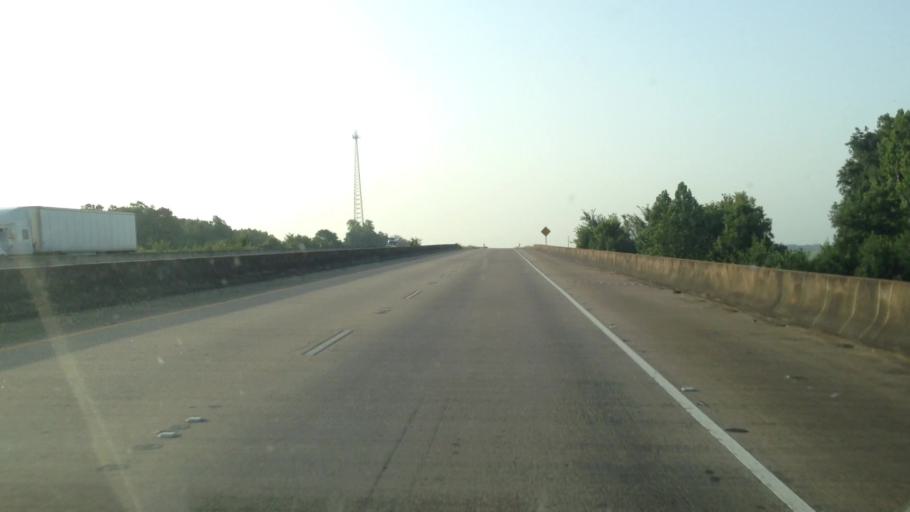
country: US
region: Louisiana
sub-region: Rapides Parish
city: Boyce
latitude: 31.3946
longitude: -92.6962
